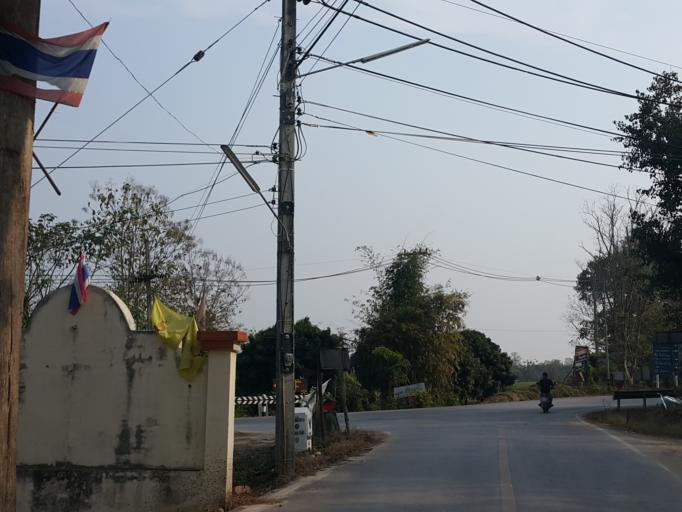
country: TH
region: Lampang
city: Chae Hom
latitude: 18.7205
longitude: 99.5618
